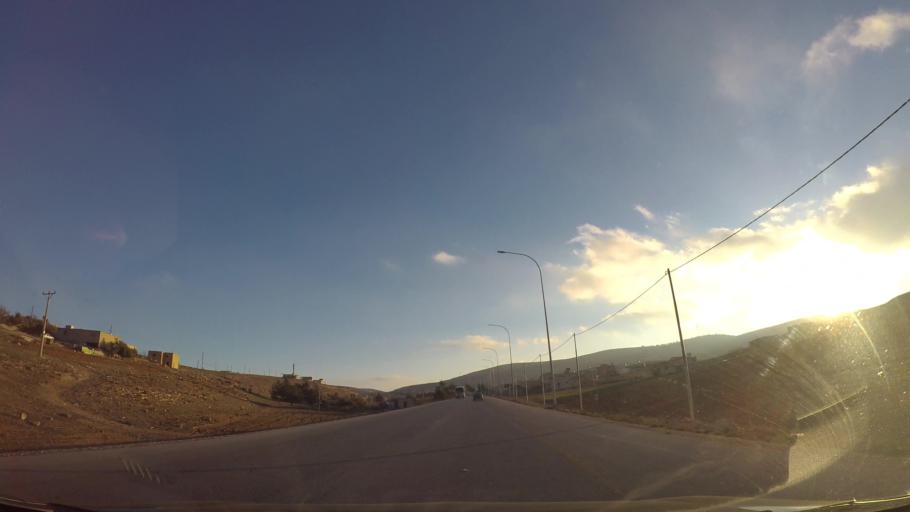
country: JO
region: Ma'an
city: Petra
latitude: 30.4423
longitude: 35.5204
